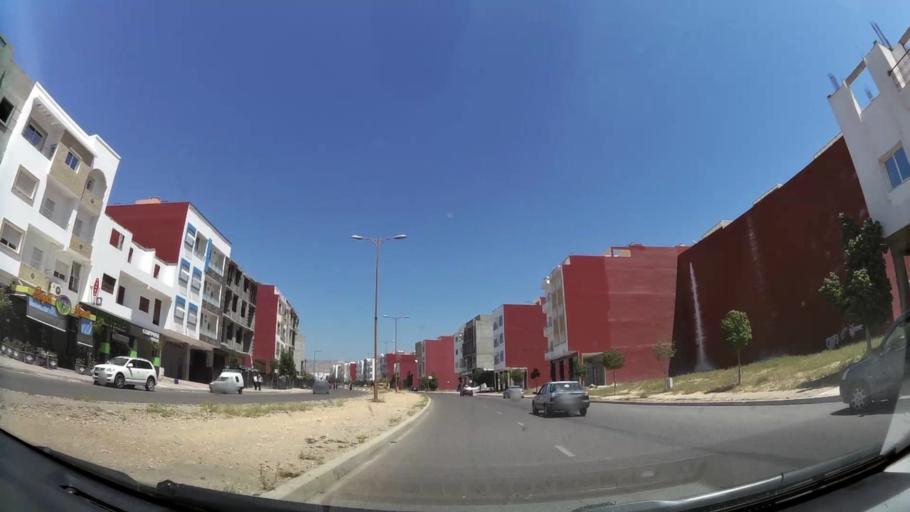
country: MA
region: Oued ed Dahab-Lagouira
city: Dakhla
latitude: 30.4296
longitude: -9.5559
